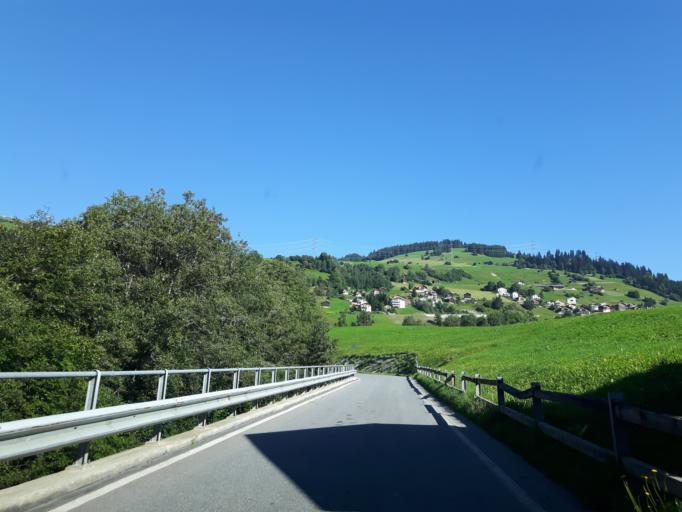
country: CH
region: Grisons
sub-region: Surselva District
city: Breil
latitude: 46.7754
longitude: 9.1091
